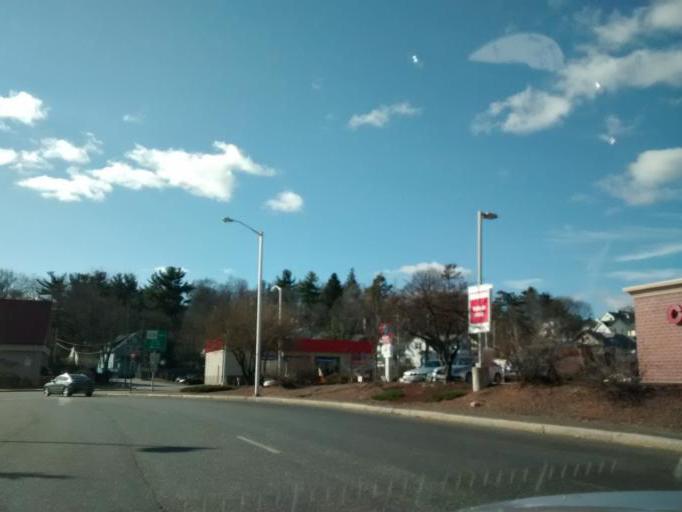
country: US
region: Massachusetts
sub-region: Worcester County
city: Worcester
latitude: 42.2892
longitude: -71.8062
